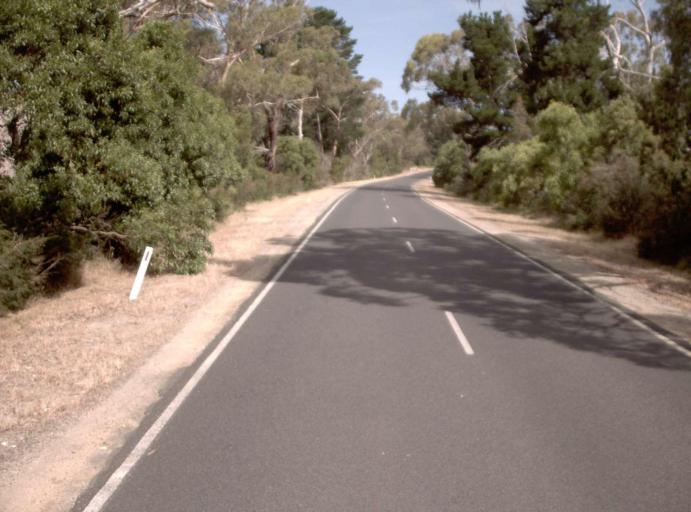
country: AU
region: Victoria
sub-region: Wellington
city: Sale
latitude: -38.2334
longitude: 147.1234
